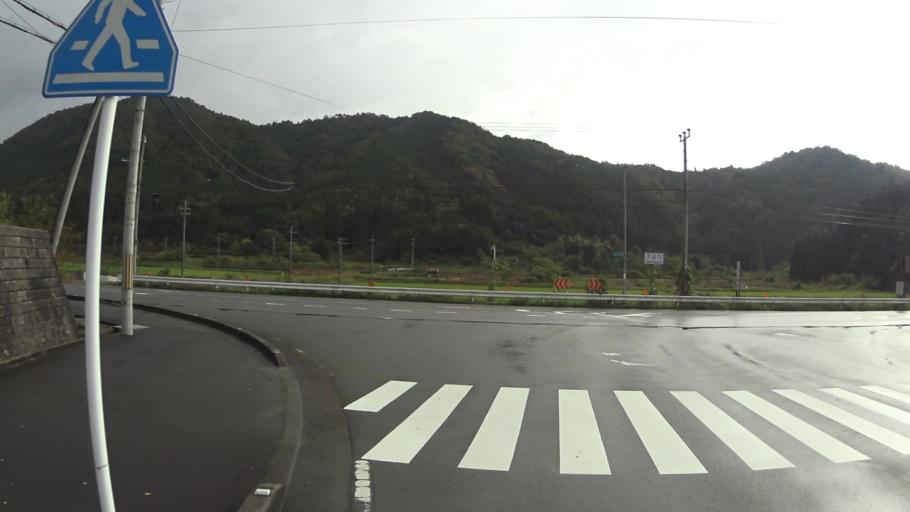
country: JP
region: Kyoto
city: Fukuchiyama
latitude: 35.4050
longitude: 135.1499
